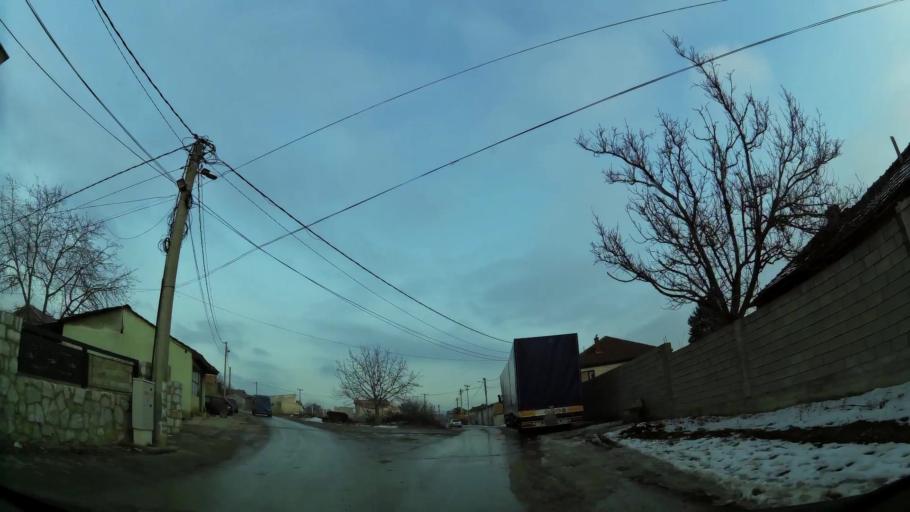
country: MK
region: Aracinovo
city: Arachinovo
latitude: 42.0226
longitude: 21.5692
